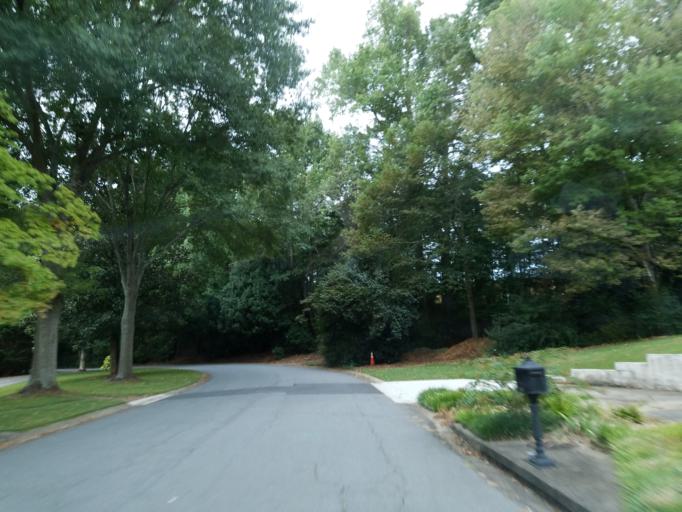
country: US
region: Georgia
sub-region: Fulton County
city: Sandy Springs
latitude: 33.9707
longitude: -84.4176
